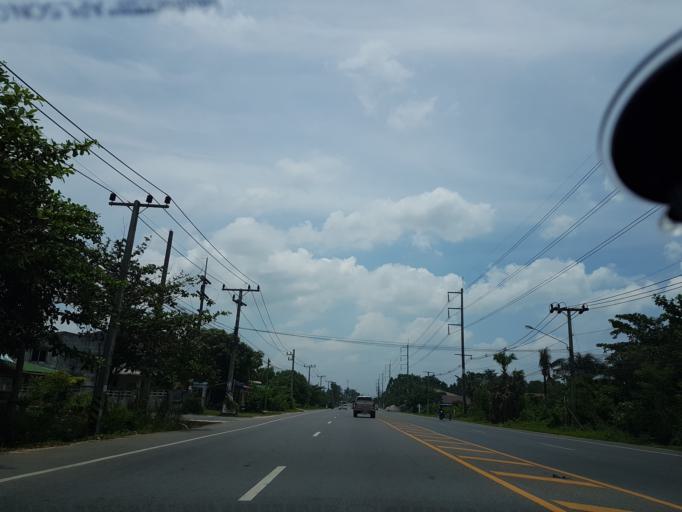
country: TH
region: Songkhla
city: Songkhla
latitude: 7.1268
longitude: 100.6313
